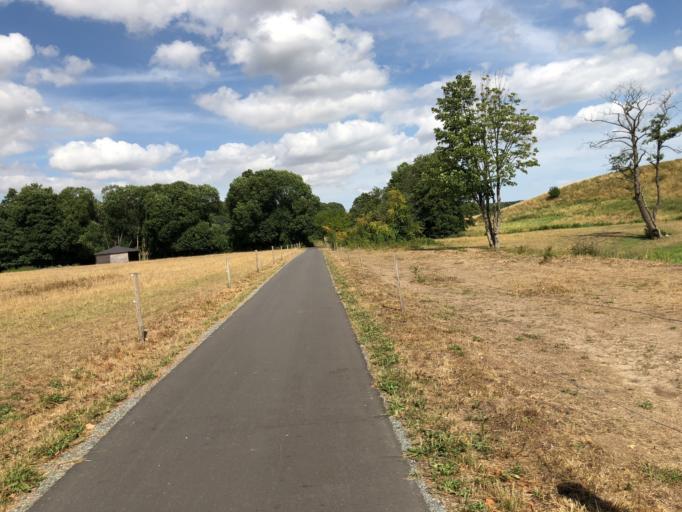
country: DK
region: South Denmark
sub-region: Vejle Kommune
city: Jelling
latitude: 55.6906
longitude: 9.4082
